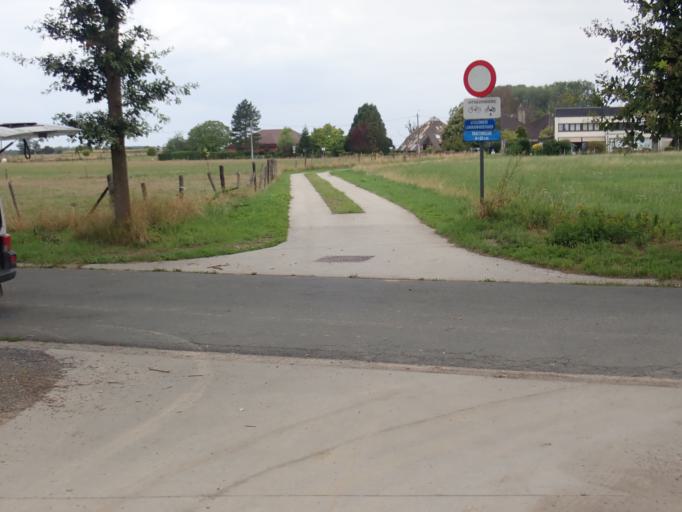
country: BE
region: Flanders
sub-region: Provincie Vlaams-Brabant
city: Merchtem
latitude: 50.9807
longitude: 4.2208
